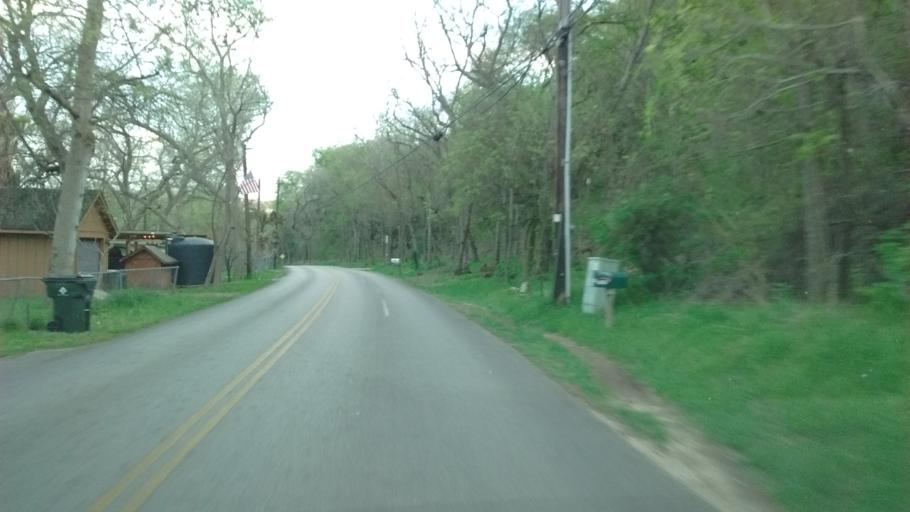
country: US
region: Texas
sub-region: Comal County
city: New Braunfels
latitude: 29.7904
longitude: -98.1523
